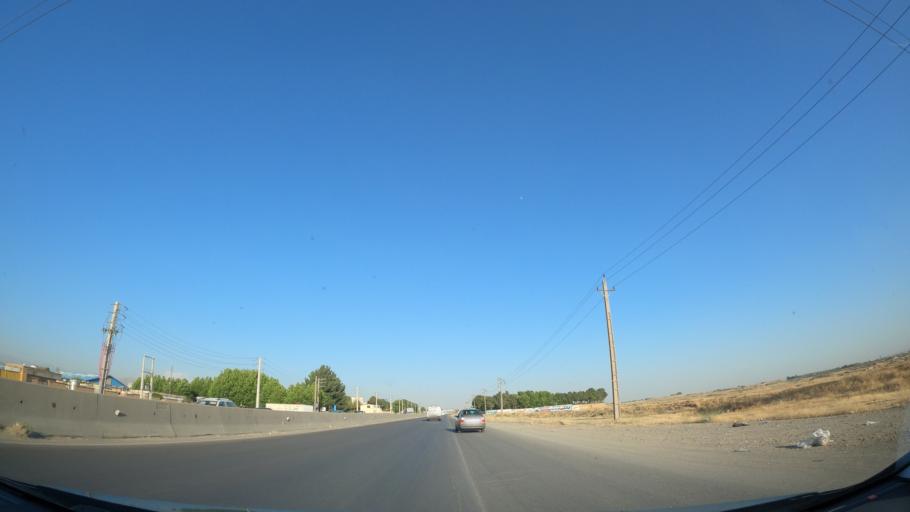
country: IR
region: Alborz
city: Hashtgerd
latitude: 35.9228
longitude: 50.7431
